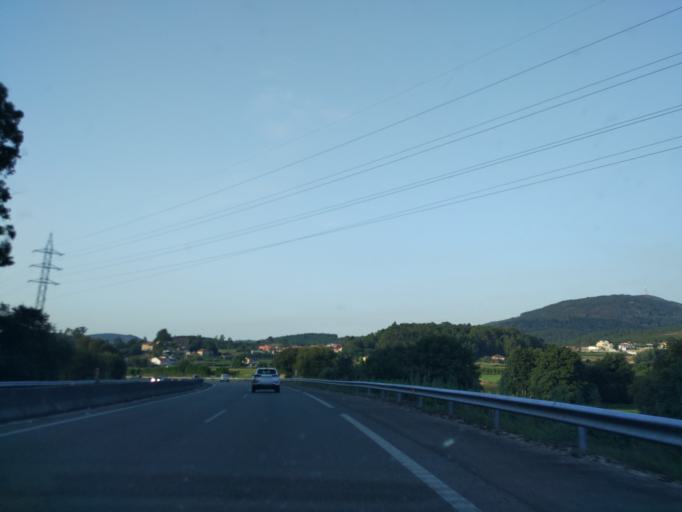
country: ES
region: Galicia
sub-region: Provincia de Pontevedra
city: Valga
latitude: 42.6626
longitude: -8.6353
